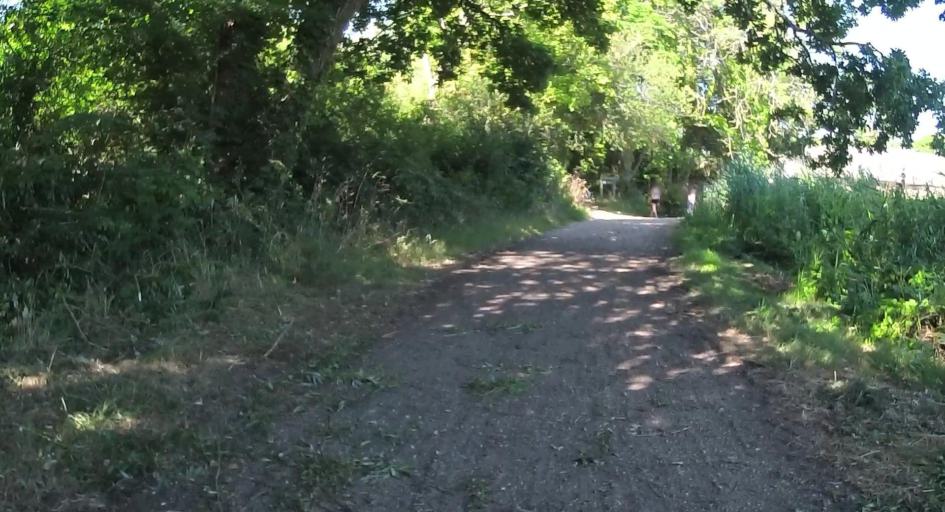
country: GB
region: England
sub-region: Dorset
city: Bovington Camp
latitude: 50.7398
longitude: -2.2425
